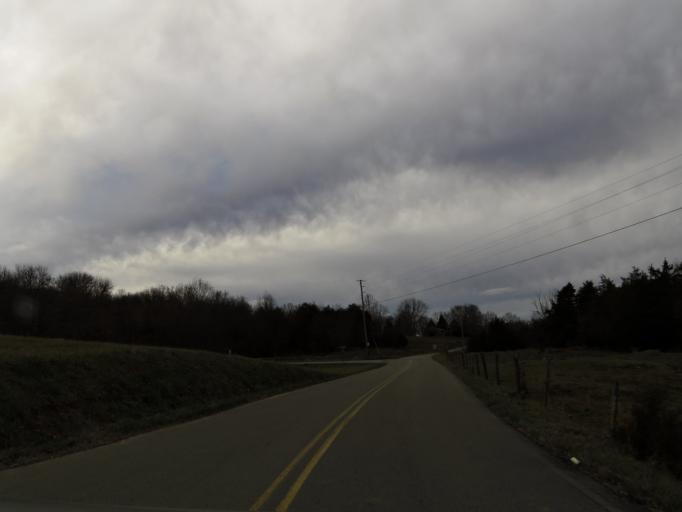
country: US
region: Tennessee
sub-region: Greene County
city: Tusculum
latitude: 36.2085
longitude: -82.7479
